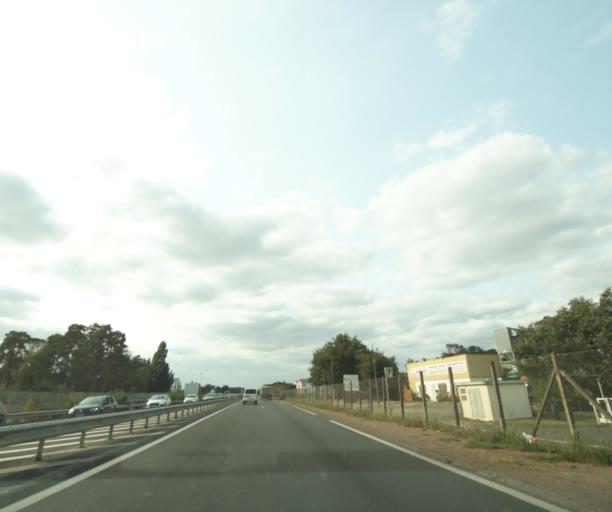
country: FR
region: Centre
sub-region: Departement d'Indre-et-Loire
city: Esvres
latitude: 47.2997
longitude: 0.7985
